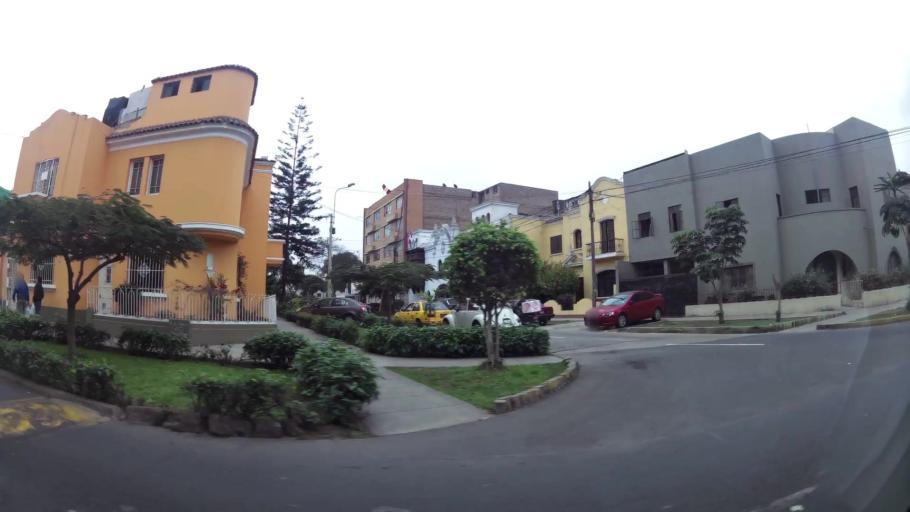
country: PE
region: Lima
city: Lima
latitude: -12.0738
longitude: -77.0445
